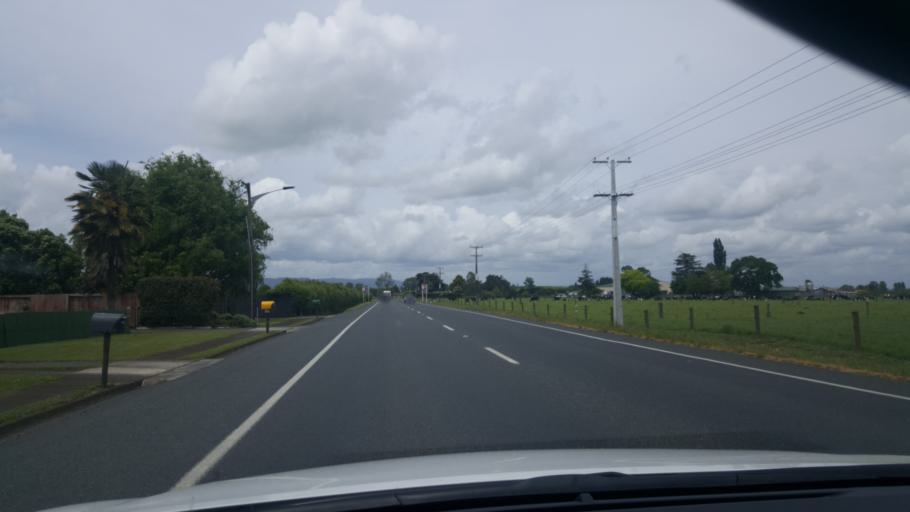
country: NZ
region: Waikato
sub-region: Matamata-Piako District
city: Matamata
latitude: -37.8839
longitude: 175.7635
